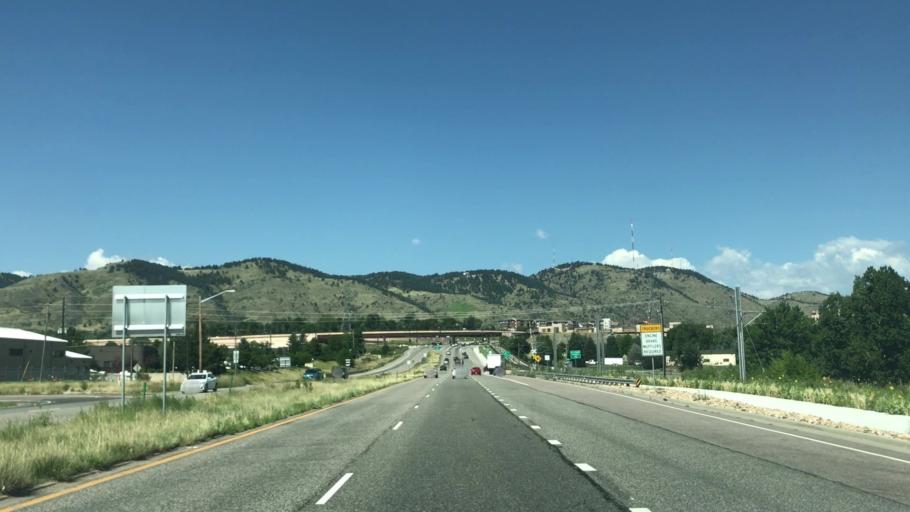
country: US
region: Colorado
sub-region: Jefferson County
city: West Pleasant View
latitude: 39.7253
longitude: -105.1919
